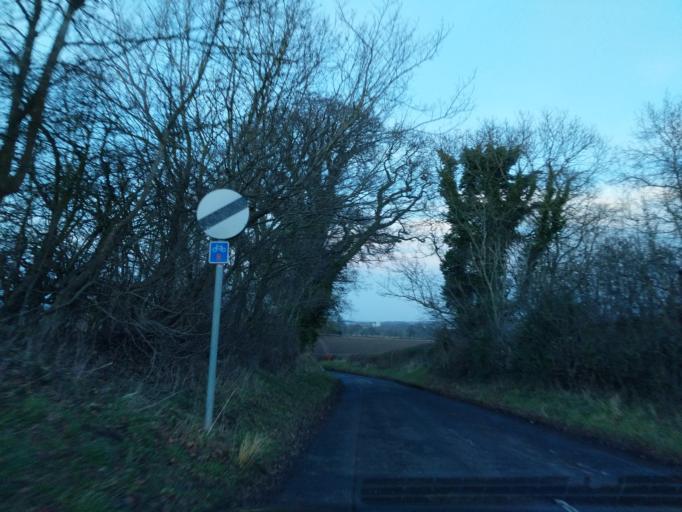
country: GB
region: Scotland
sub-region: Midlothian
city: Bonnyrigg
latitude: 55.8342
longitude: -3.0876
